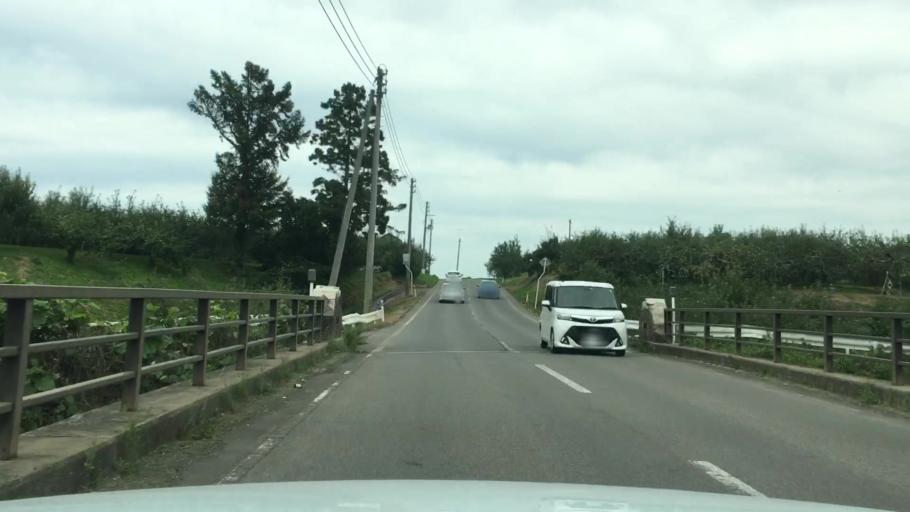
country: JP
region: Aomori
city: Hirosaki
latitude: 40.6558
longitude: 140.4205
